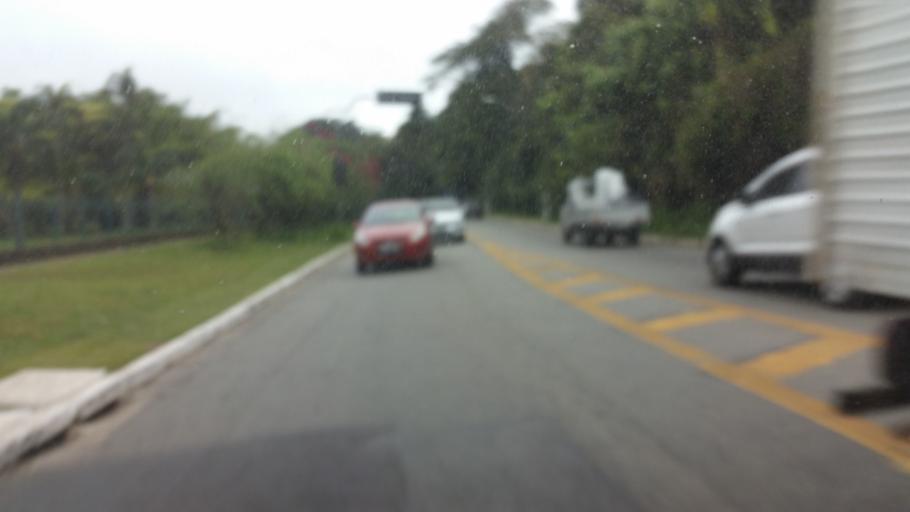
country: BR
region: Sao Paulo
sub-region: Diadema
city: Diadema
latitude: -23.6396
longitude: -46.6274
